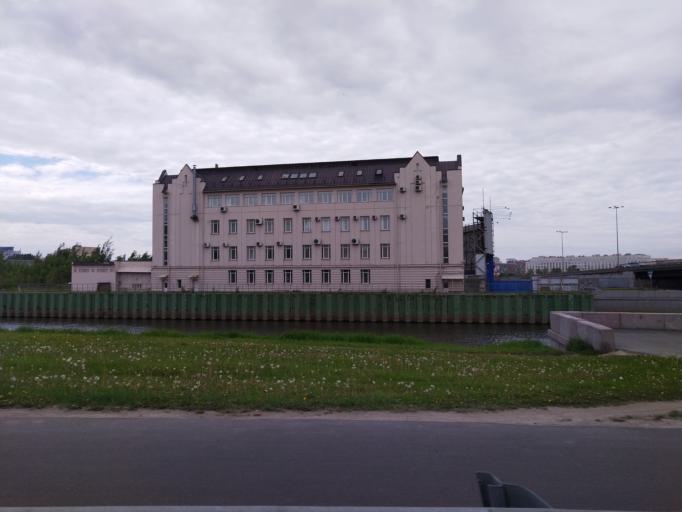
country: RU
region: Leningrad
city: Finlyandskiy
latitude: 59.9462
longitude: 30.4079
